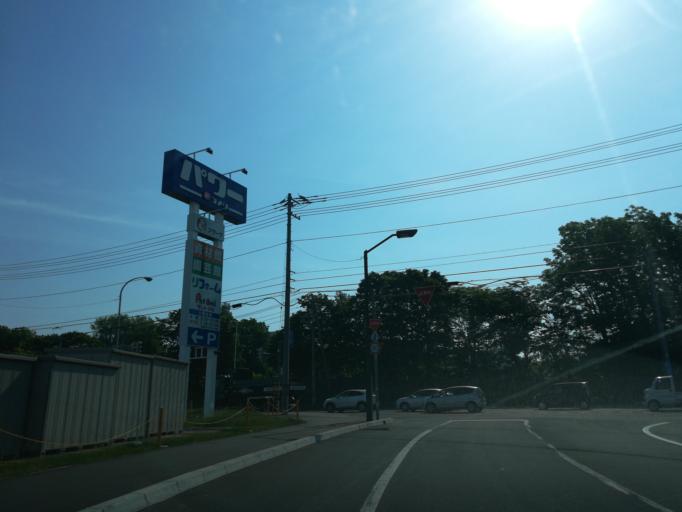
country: JP
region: Hokkaido
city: Iwamizawa
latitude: 43.2144
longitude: 141.7840
